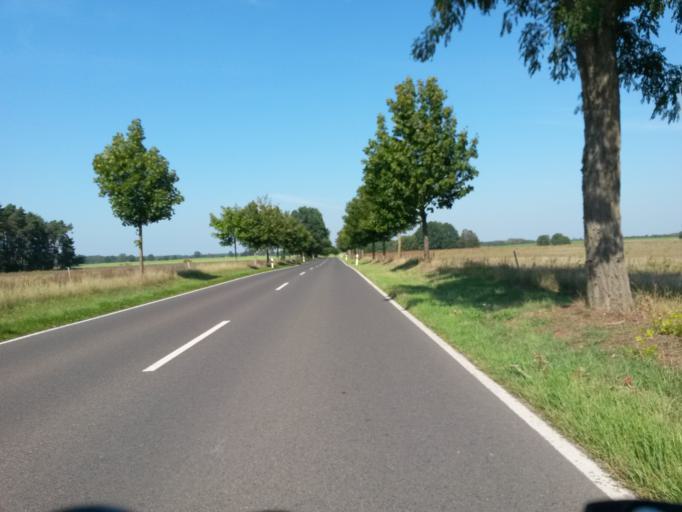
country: DE
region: Brandenburg
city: Templin
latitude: 53.0573
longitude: 13.4370
